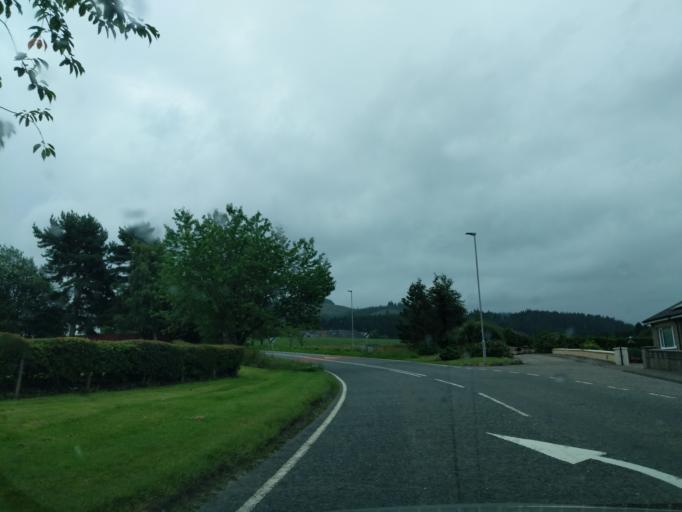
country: GB
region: Scotland
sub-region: Moray
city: Rothes
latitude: 57.4856
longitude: -3.1842
